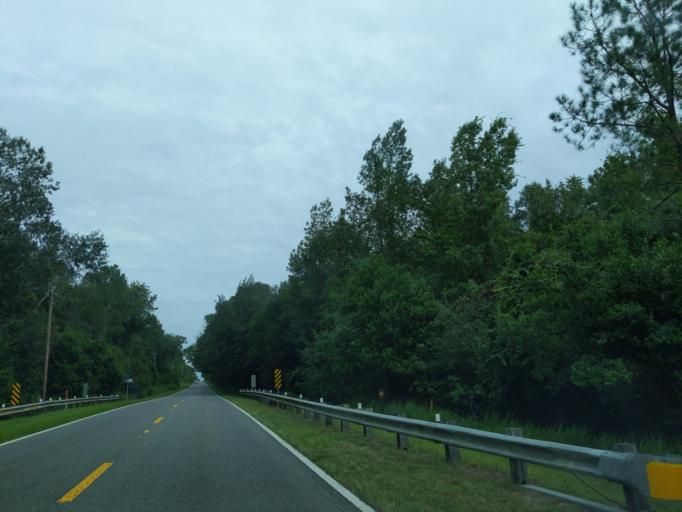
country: US
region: Florida
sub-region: Leon County
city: Woodville
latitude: 30.3770
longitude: -84.2207
